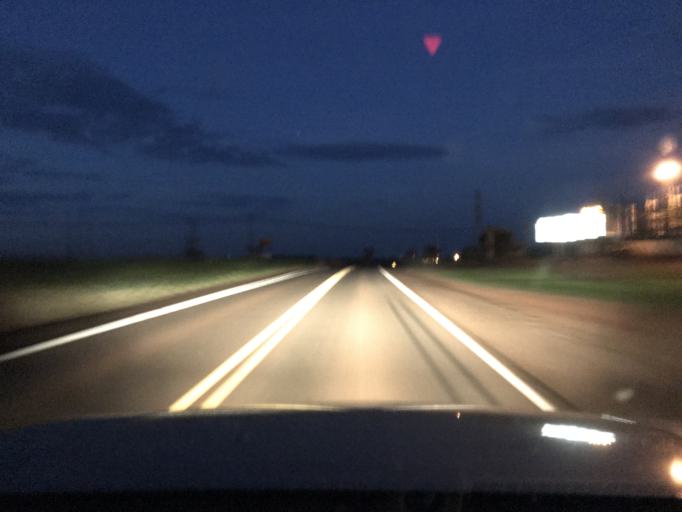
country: PY
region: Canindeyu
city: Salto del Guaira
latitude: -24.1016
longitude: -54.2286
